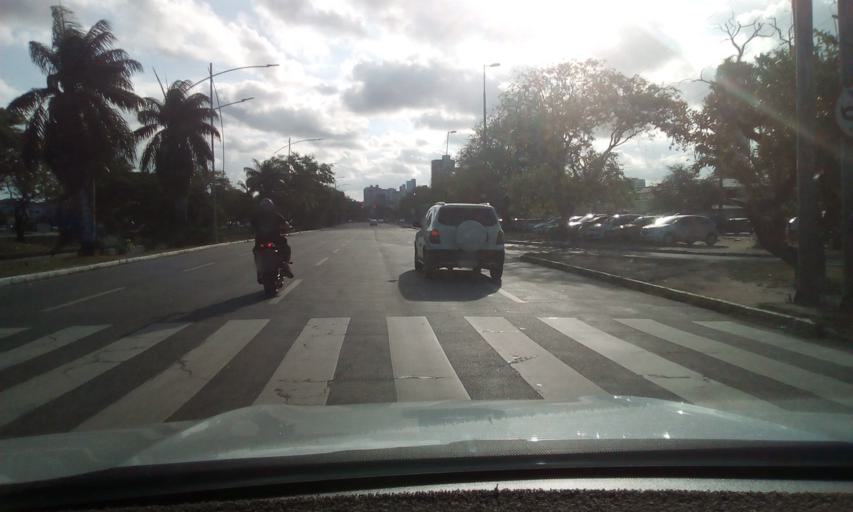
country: BR
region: Pernambuco
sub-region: Recife
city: Recife
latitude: -8.0395
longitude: -34.8789
